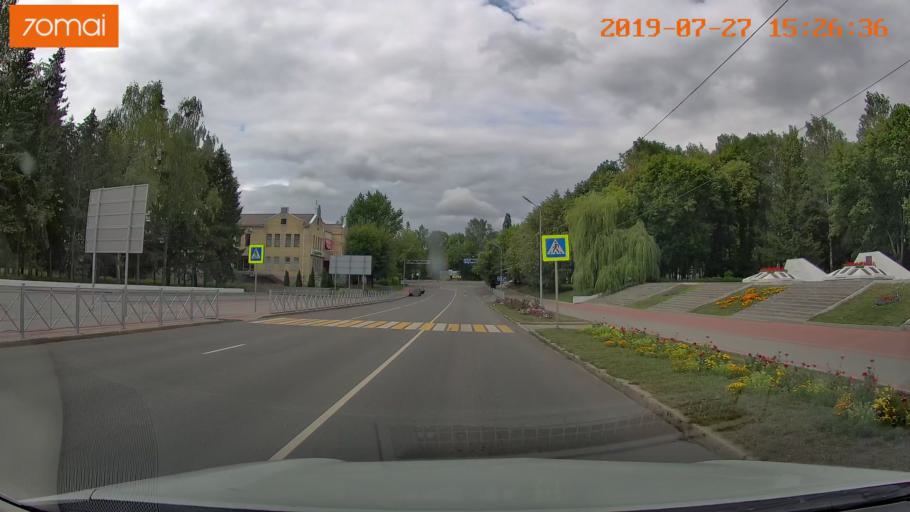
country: RU
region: Kaliningrad
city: Nesterov
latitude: 54.6316
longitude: 22.5713
